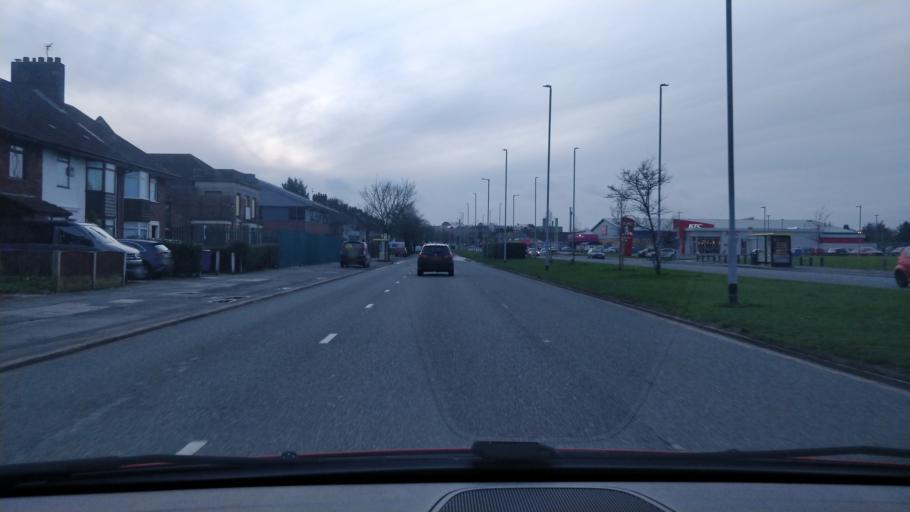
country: GB
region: England
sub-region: Knowsley
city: Huyton
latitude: 53.4195
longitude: -2.8813
